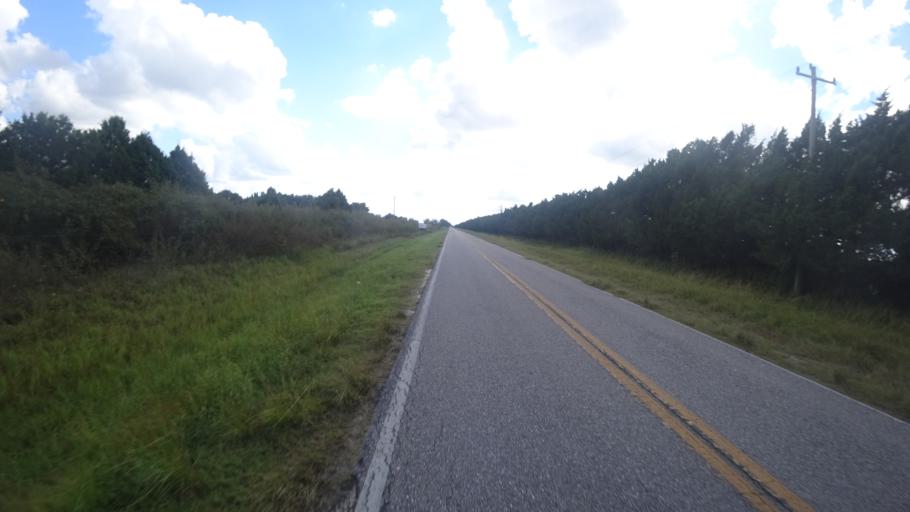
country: US
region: Florida
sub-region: DeSoto County
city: Arcadia
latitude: 27.2965
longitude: -82.1134
